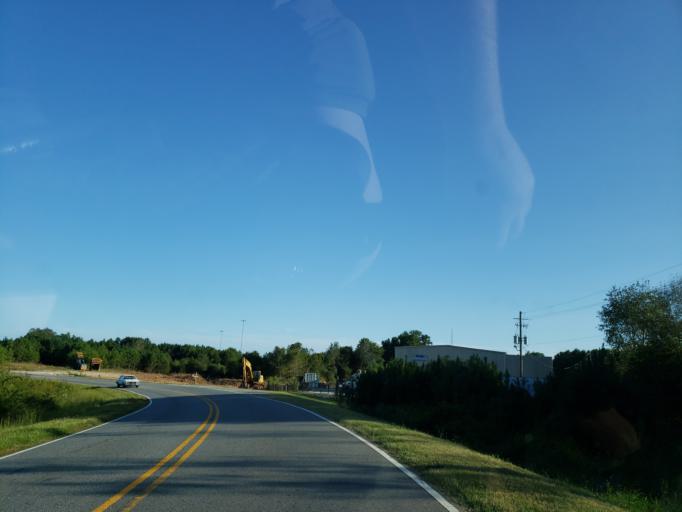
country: US
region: Georgia
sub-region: Bartow County
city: Rydal
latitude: 34.2790
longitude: -84.8113
